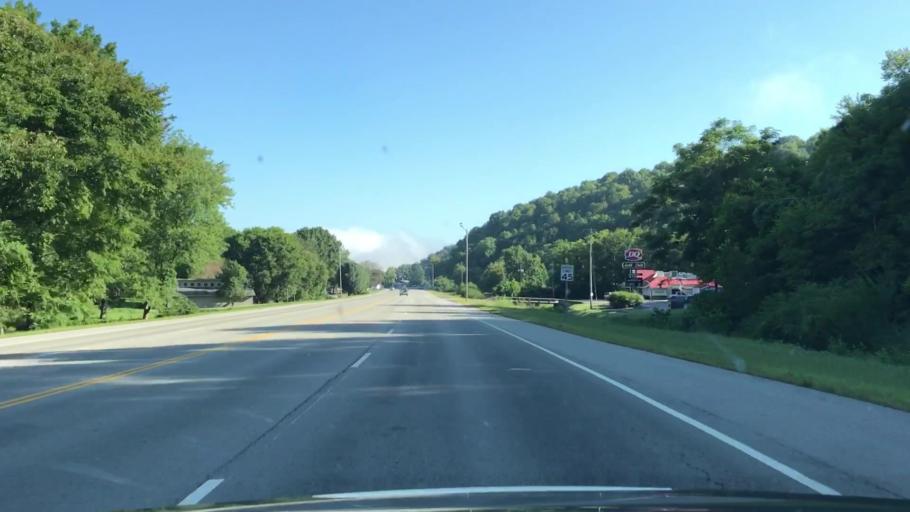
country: US
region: Tennessee
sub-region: Jackson County
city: Gainesboro
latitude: 36.3516
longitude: -85.6560
